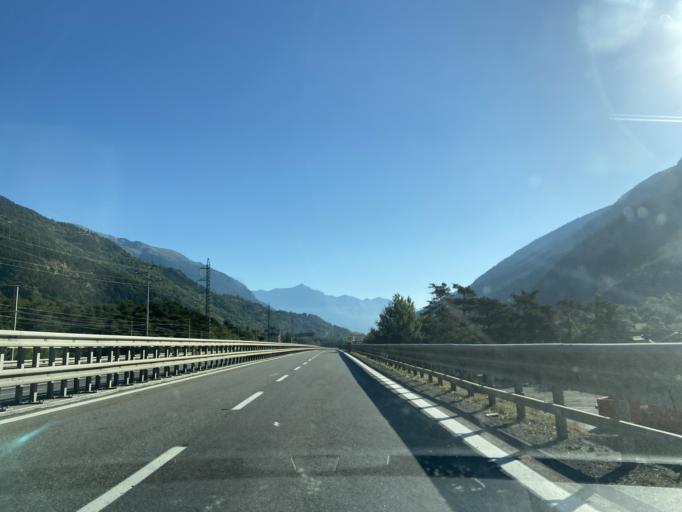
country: IT
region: Piedmont
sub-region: Provincia di Torino
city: Salbertrand
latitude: 45.0645
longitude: 6.8753
